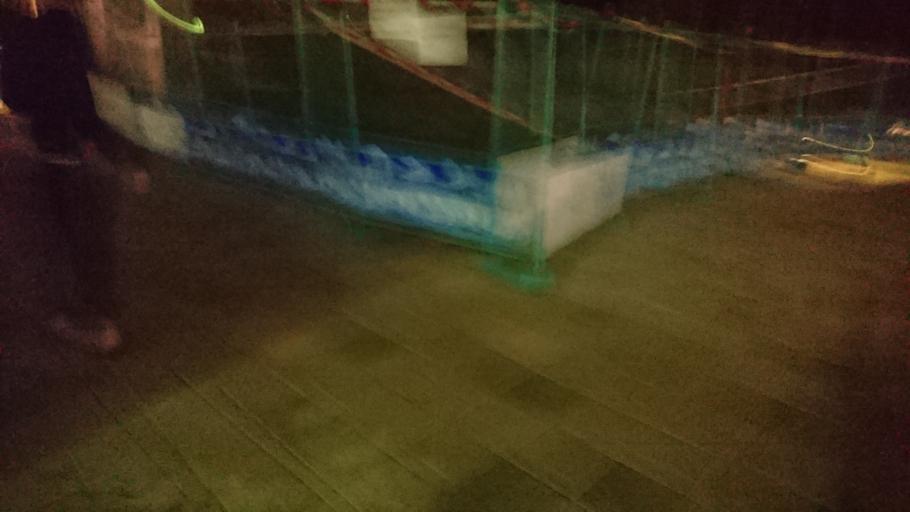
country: TW
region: Taiwan
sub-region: Hsinchu
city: Hsinchu
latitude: 24.7987
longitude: 120.9790
